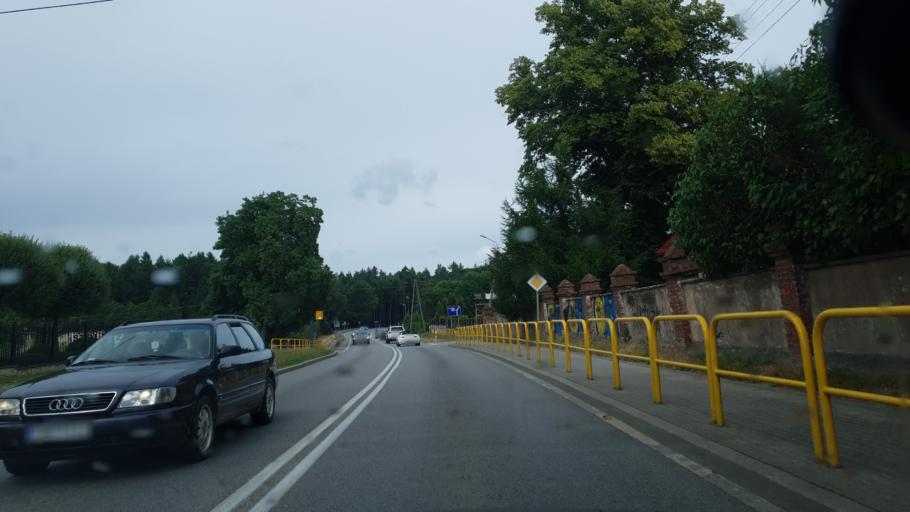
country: PL
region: Pomeranian Voivodeship
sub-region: Powiat kartuski
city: Chwaszczyno
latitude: 54.4294
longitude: 18.3901
